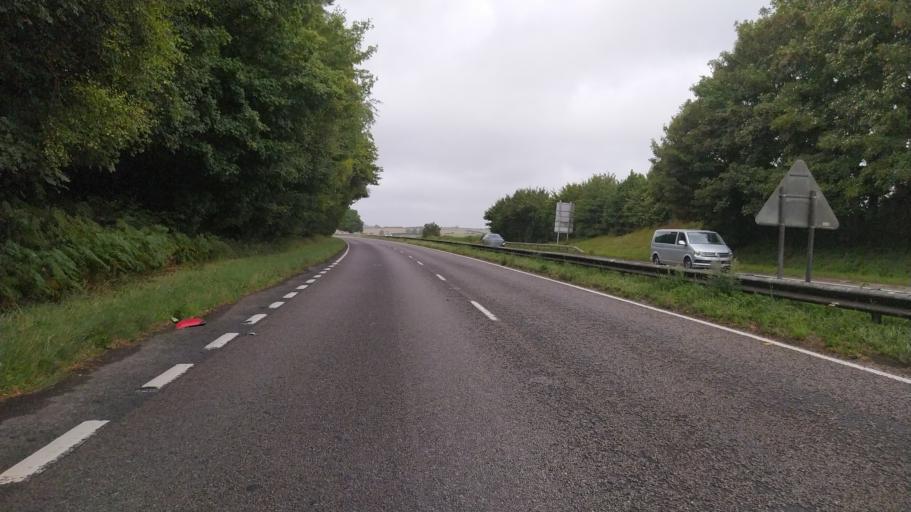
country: GB
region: England
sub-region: Dorset
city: Bovington Camp
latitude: 50.7560
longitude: -2.2353
